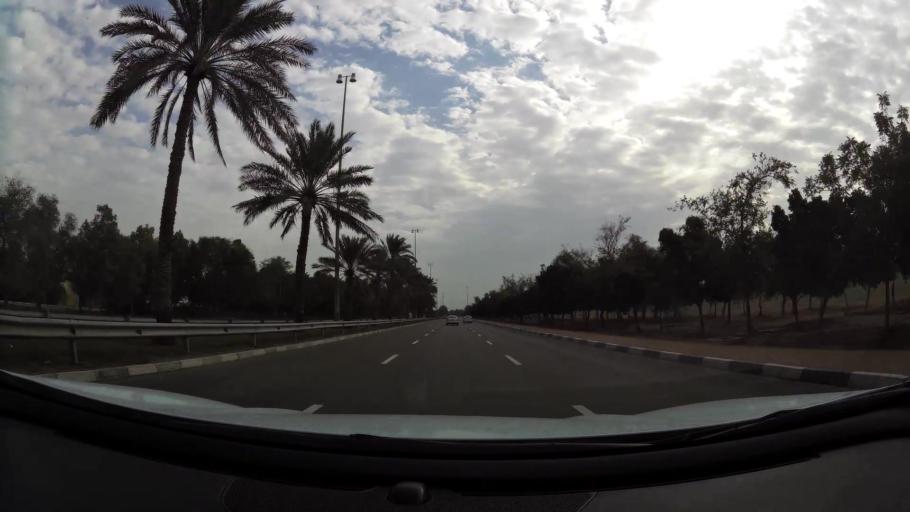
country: AE
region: Abu Dhabi
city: Al Ain
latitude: 24.1776
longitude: 55.6151
